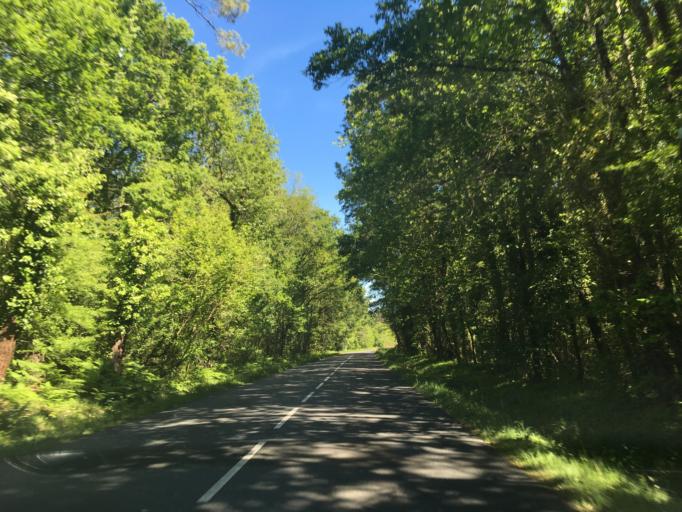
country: FR
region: Aquitaine
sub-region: Departement de la Gironde
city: Lesparre-Medoc
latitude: 45.2850
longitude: -0.8959
